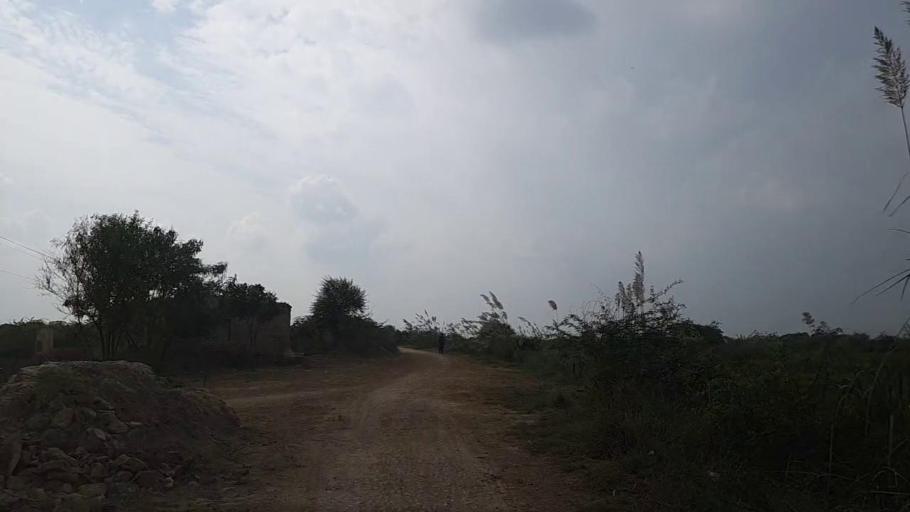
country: PK
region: Sindh
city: Mirpur Batoro
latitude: 24.5982
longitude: 68.1325
